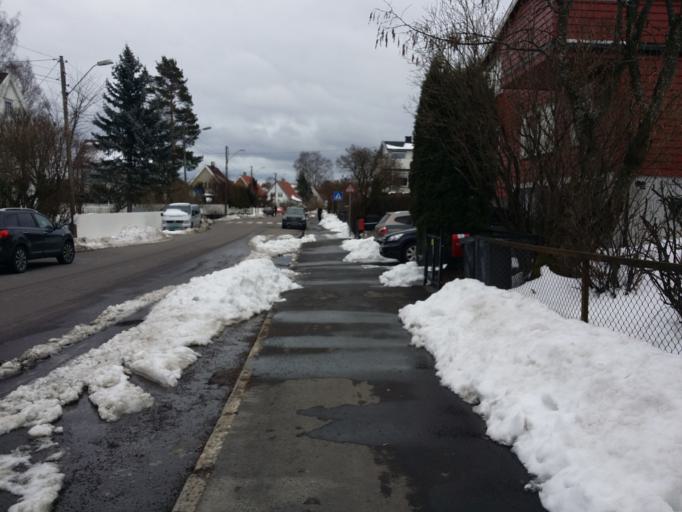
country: NO
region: Oslo
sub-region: Oslo
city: Oslo
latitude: 59.8980
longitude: 10.7776
